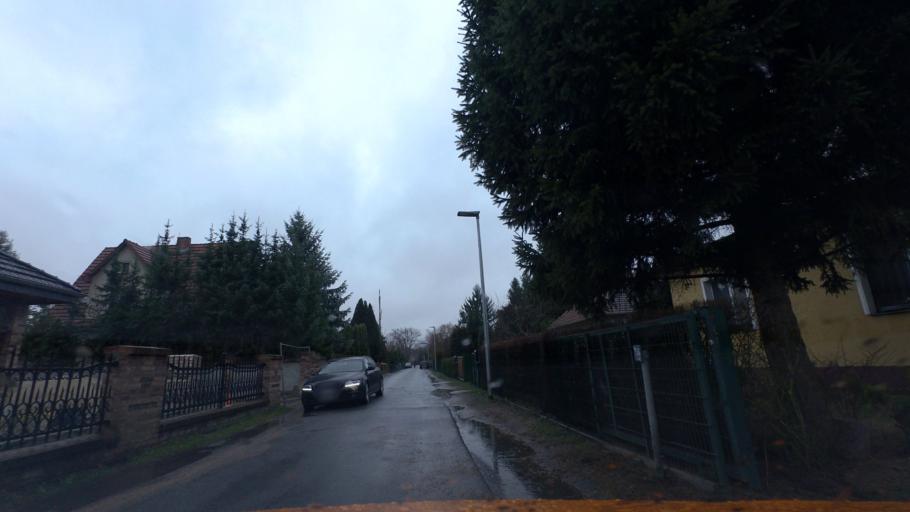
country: DE
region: Brandenburg
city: Brieselang
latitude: 52.5859
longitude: 13.0019
